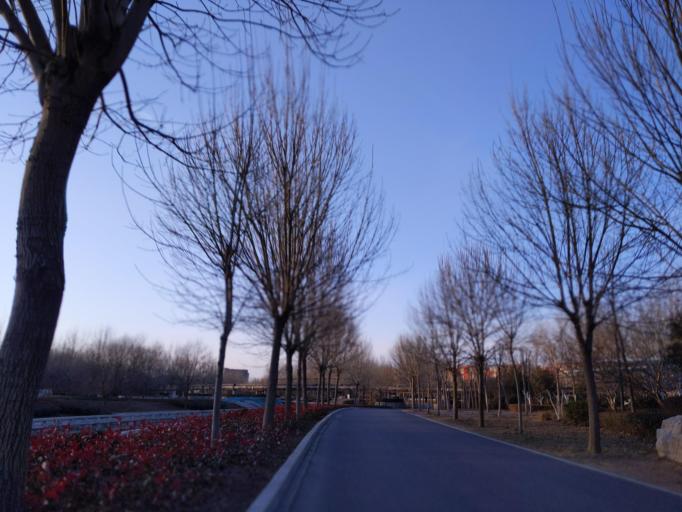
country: CN
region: Henan Sheng
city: Puyang
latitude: 35.7689
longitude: 114.9988
